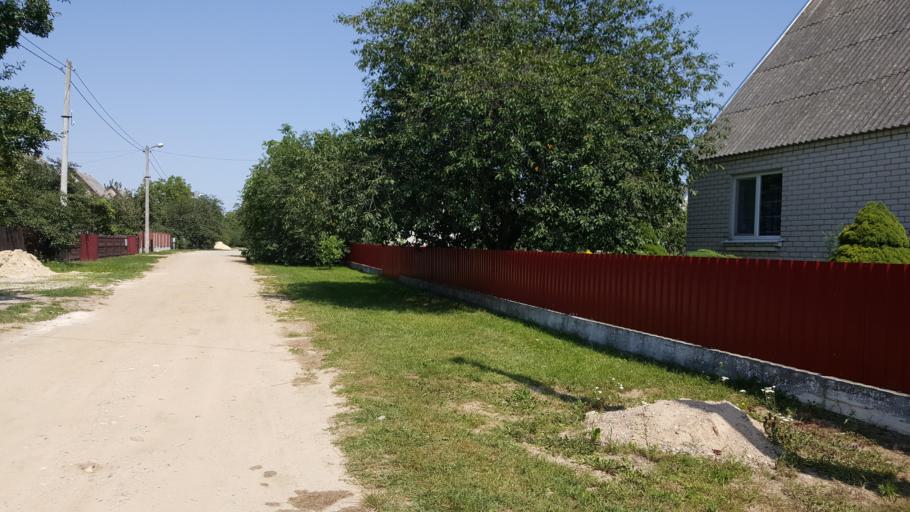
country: BY
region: Brest
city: Zhabinka
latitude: 52.1907
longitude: 24.0026
